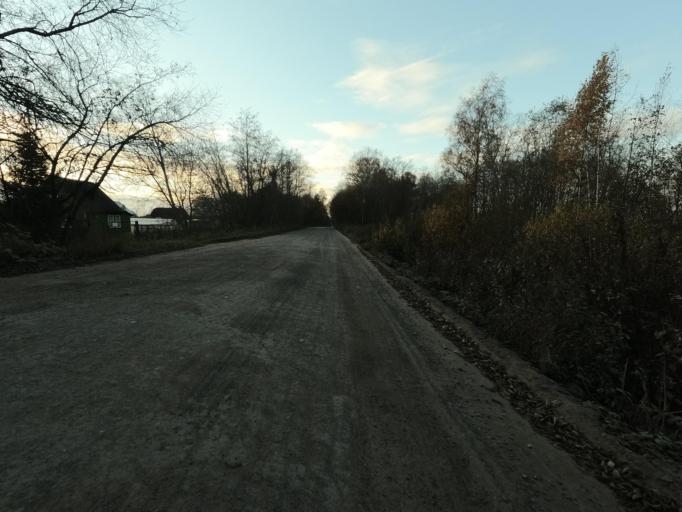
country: RU
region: Leningrad
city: Mga
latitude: 59.7658
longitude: 31.2440
